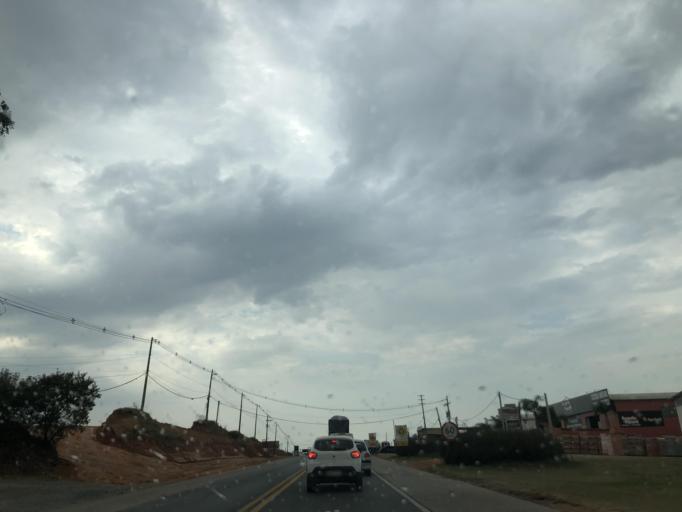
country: BR
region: Sao Paulo
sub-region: Salto De Pirapora
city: Salto de Pirapora
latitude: -23.6469
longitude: -47.5837
